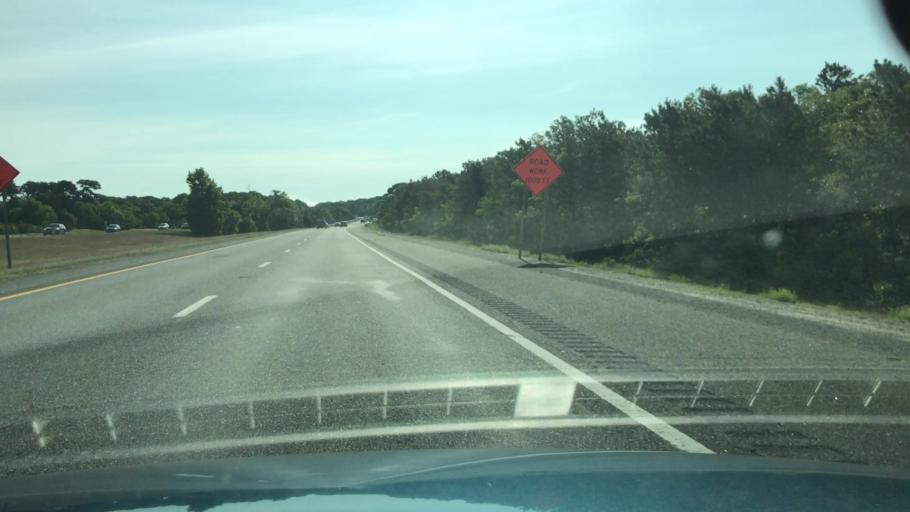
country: US
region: Massachusetts
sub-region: Barnstable County
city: South Dennis
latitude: 41.6929
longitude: -70.1742
